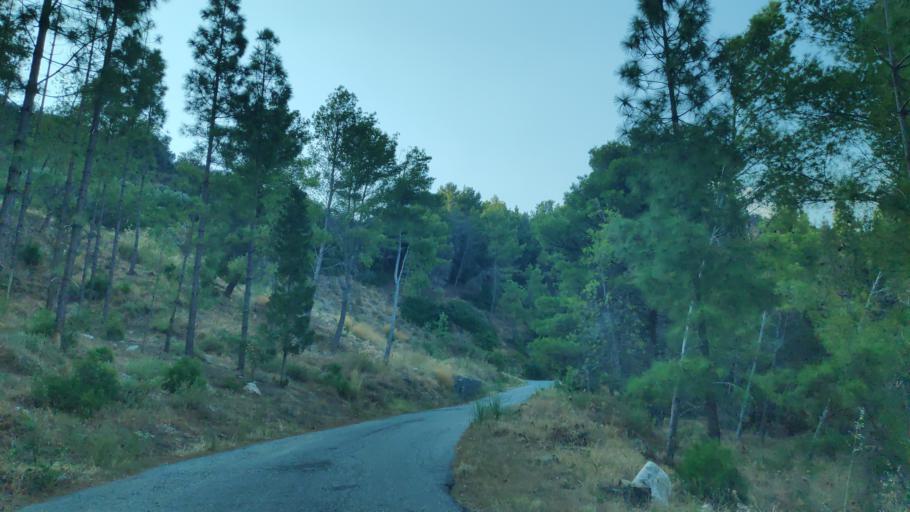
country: IT
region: Calabria
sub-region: Provincia di Reggio Calabria
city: Placanica
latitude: 38.4105
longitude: 16.4304
